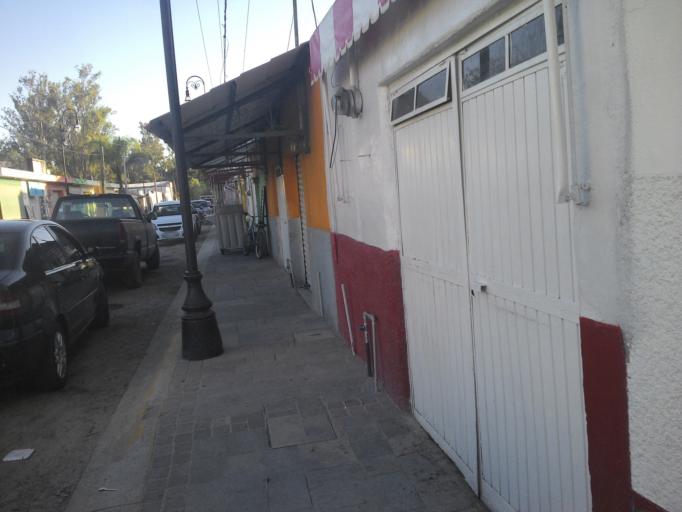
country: MX
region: Jalisco
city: San Diego de Alejandria
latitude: 20.8795
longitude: -101.9819
